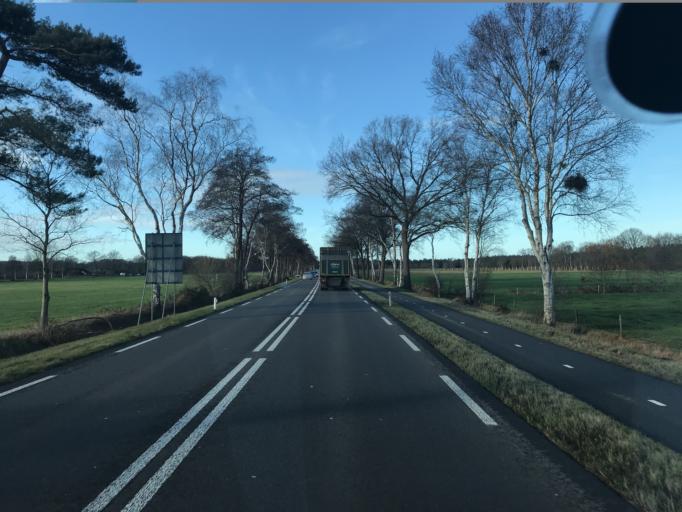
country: NL
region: Gelderland
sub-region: Gemeente Barneveld
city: Garderen
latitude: 52.2766
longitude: 5.7226
